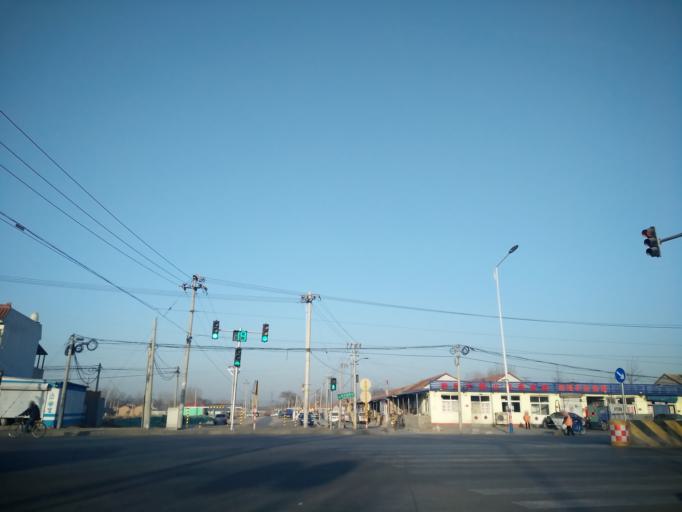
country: CN
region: Beijing
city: Weishanzhuang
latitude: 39.6666
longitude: 116.4080
